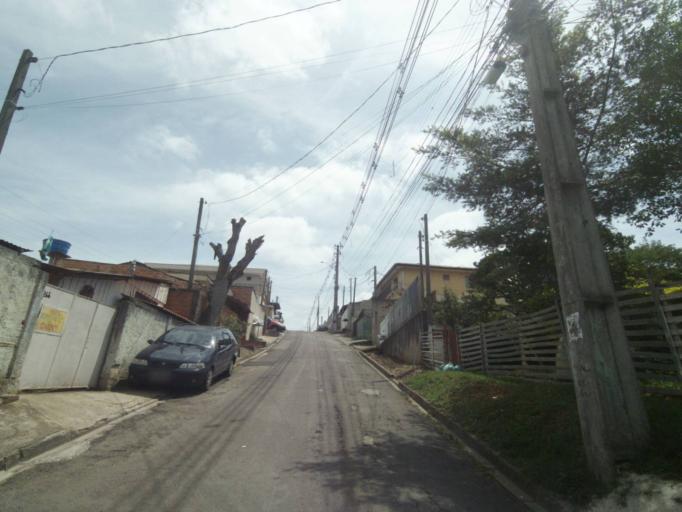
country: BR
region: Parana
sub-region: Curitiba
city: Curitiba
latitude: -25.4895
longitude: -49.3407
